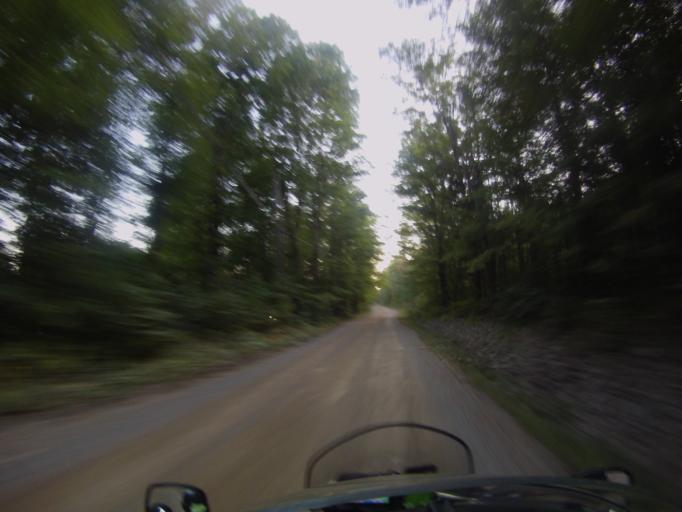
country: US
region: Vermont
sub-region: Addison County
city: Middlebury (village)
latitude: 43.9978
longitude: -73.0408
